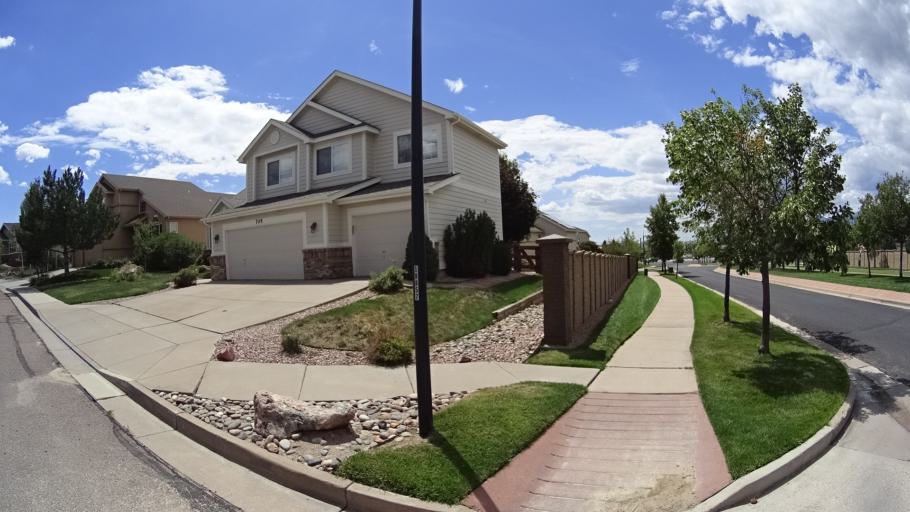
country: US
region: Colorado
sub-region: El Paso County
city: Gleneagle
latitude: 39.0287
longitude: -104.8170
